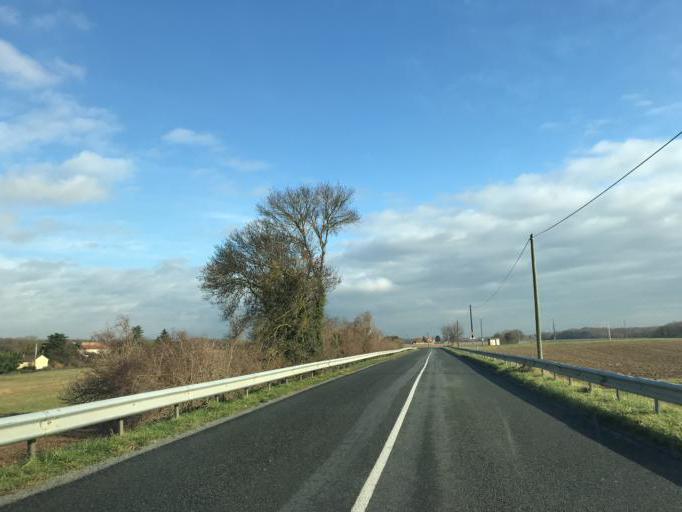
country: FR
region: Rhone-Alpes
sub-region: Departement de l'Ain
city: Civrieux
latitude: 45.9321
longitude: 4.8960
